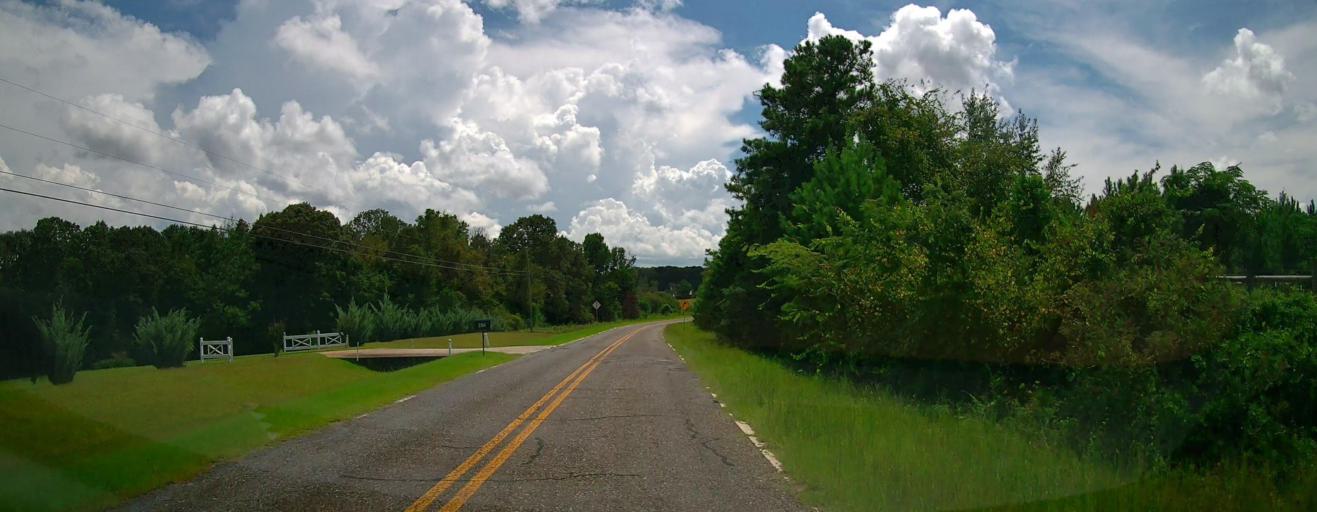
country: US
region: Georgia
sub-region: Peach County
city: Fort Valley
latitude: 32.5266
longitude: -83.8260
